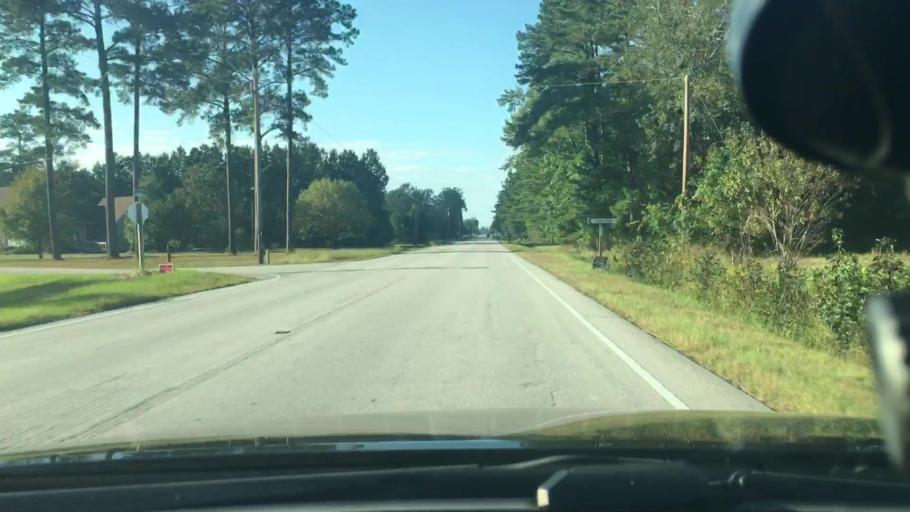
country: US
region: North Carolina
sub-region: Craven County
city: Vanceboro
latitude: 35.3585
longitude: -77.1952
